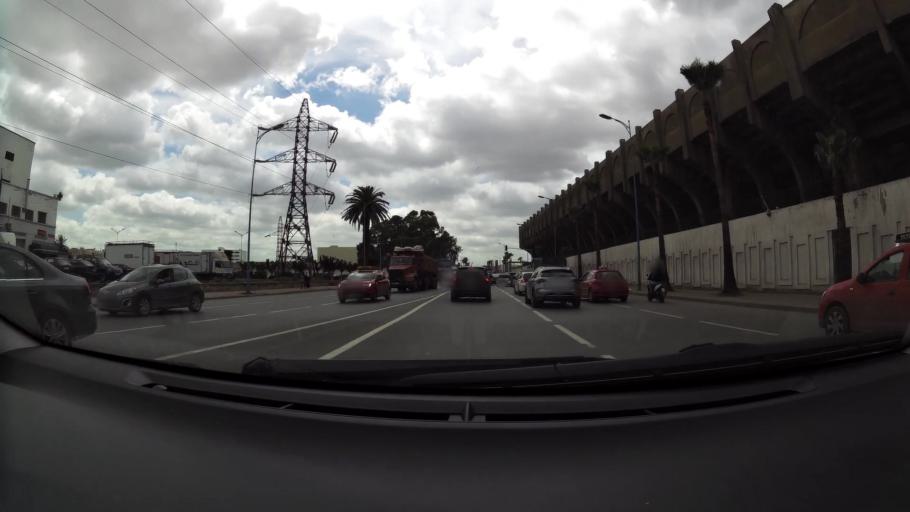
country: MA
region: Grand Casablanca
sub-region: Casablanca
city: Casablanca
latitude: 33.5978
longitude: -7.5454
